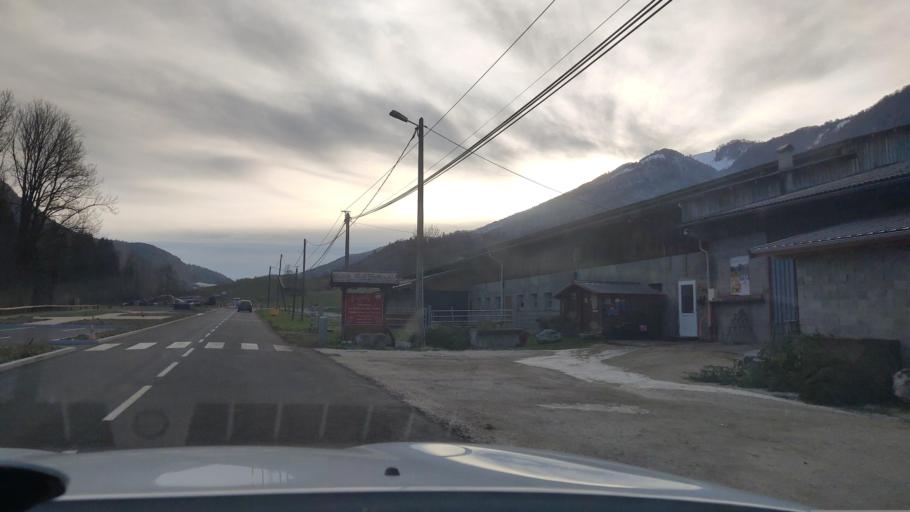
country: FR
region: Rhone-Alpes
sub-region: Departement de la Savoie
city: Coise-Saint-Jean-Pied-Gauthier
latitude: 45.6154
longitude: 6.1433
